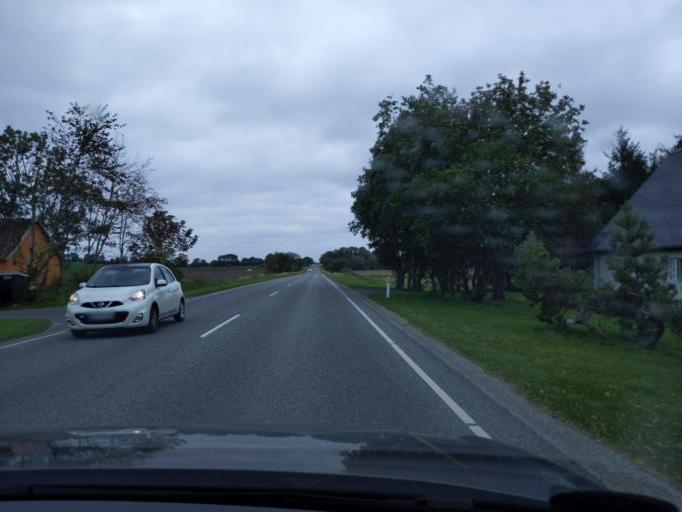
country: DK
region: Central Jutland
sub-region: Randers Kommune
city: Spentrup
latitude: 56.5302
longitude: 9.9170
